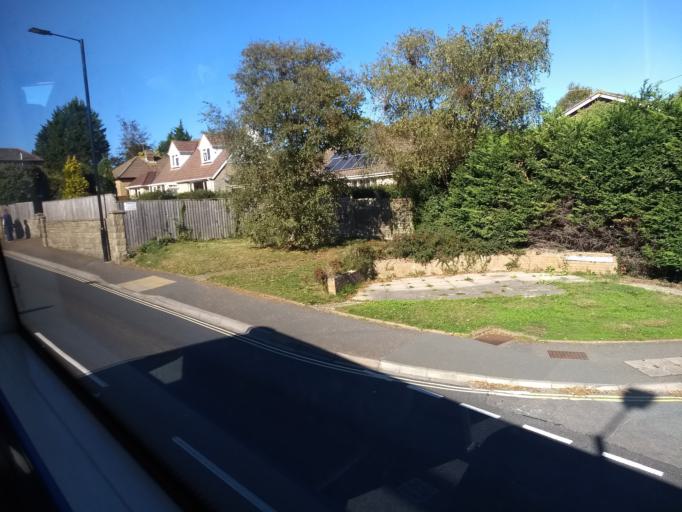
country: GB
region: England
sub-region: Isle of Wight
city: Newchurch
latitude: 50.7252
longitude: -1.2317
